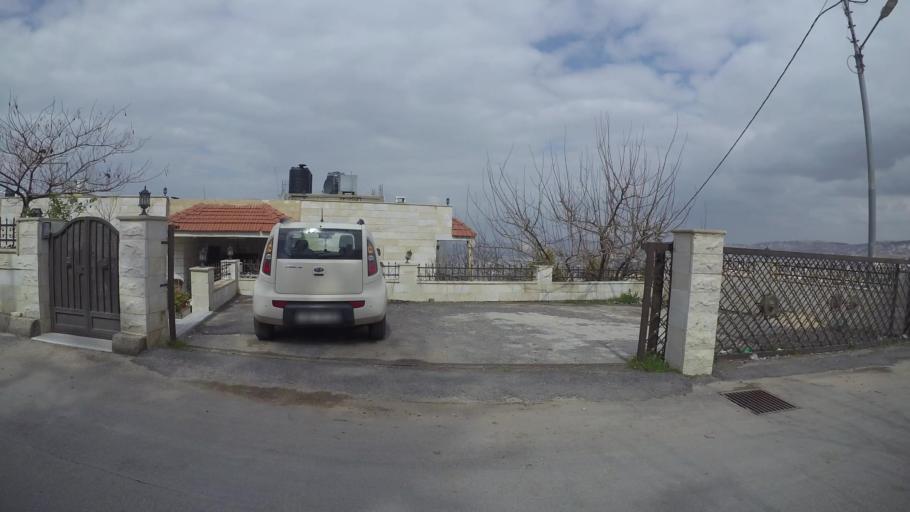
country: JO
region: Amman
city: Al Jubayhah
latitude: 32.0360
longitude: 35.8240
